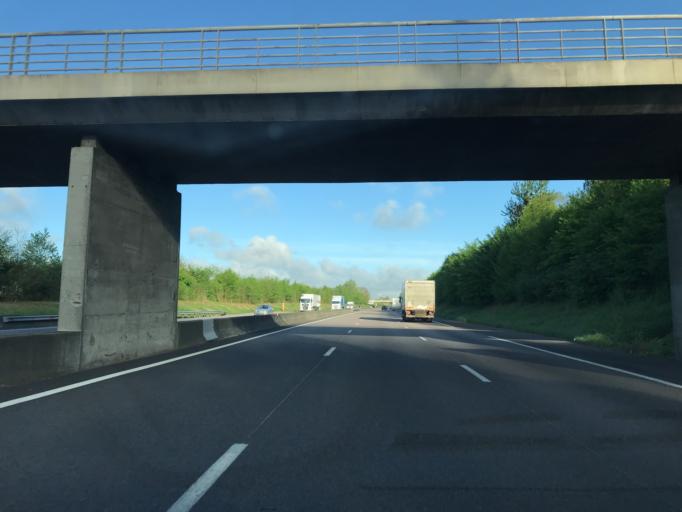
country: FR
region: Haute-Normandie
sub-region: Departement de l'Eure
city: Saint-Ouen-de-Thouberville
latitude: 49.3516
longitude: 0.8912
